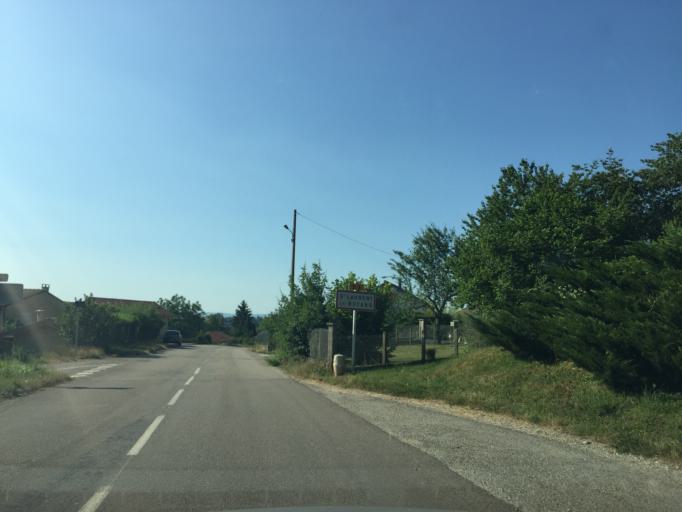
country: FR
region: Rhone-Alpes
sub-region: Departement de la Drome
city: Saint-Laurent-en-Royans
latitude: 45.0239
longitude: 5.3293
